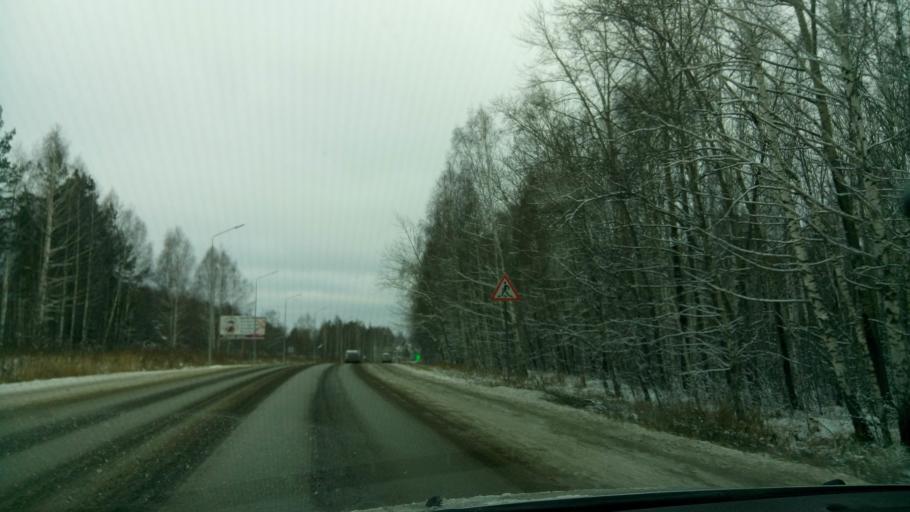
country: RU
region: Sverdlovsk
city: Polevskoy
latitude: 56.4634
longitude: 60.2214
